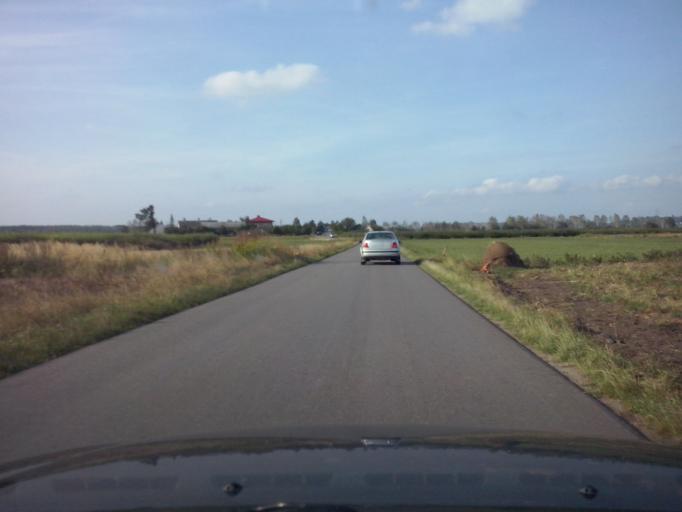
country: PL
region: Subcarpathian Voivodeship
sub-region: Powiat nizanski
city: Krzeszow
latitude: 50.3732
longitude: 22.3259
